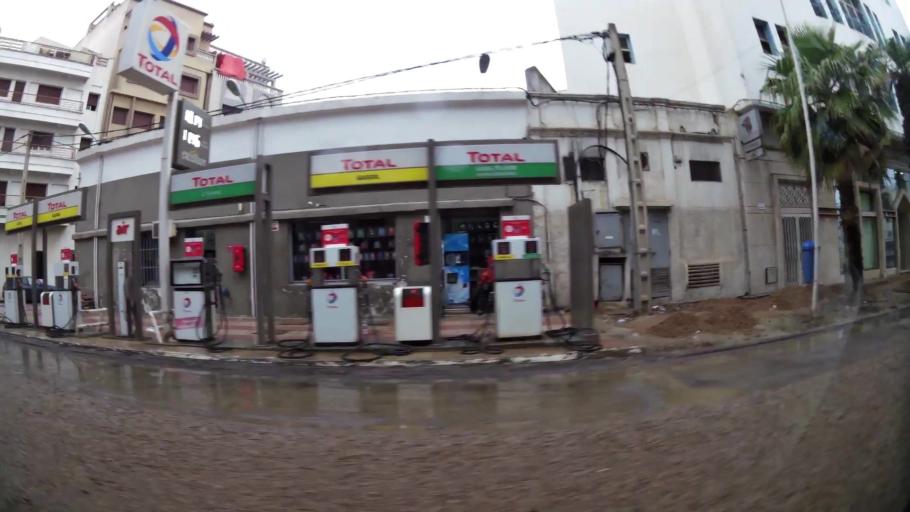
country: MA
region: Taza-Al Hoceima-Taounate
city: Al Hoceima
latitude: 35.2412
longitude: -3.9296
